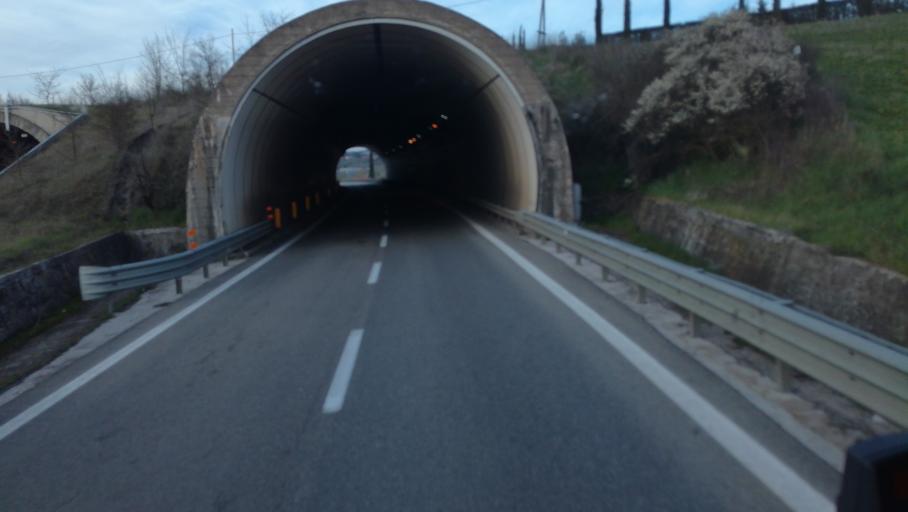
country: IT
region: Tuscany
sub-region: Provincia di Siena
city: Isola D'Arbia
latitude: 43.2729
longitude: 11.3331
